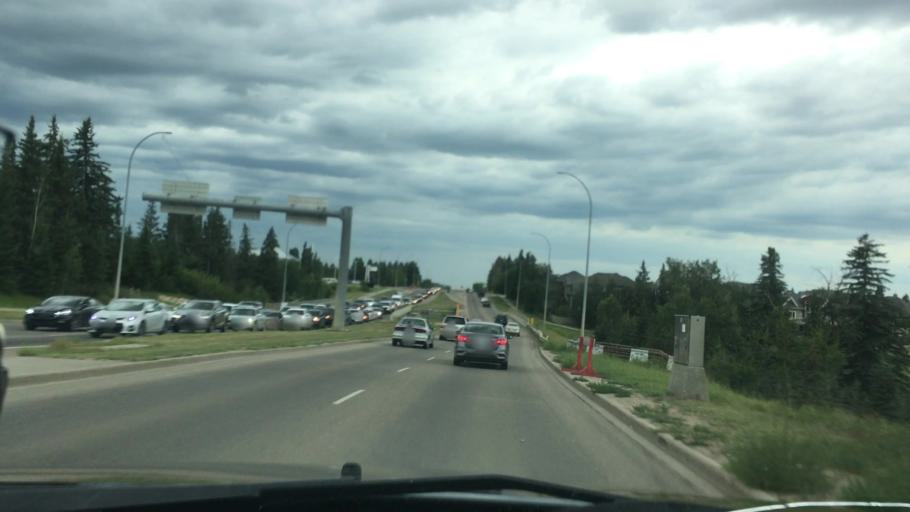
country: CA
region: Alberta
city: Beaumont
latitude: 53.4249
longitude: -113.4965
